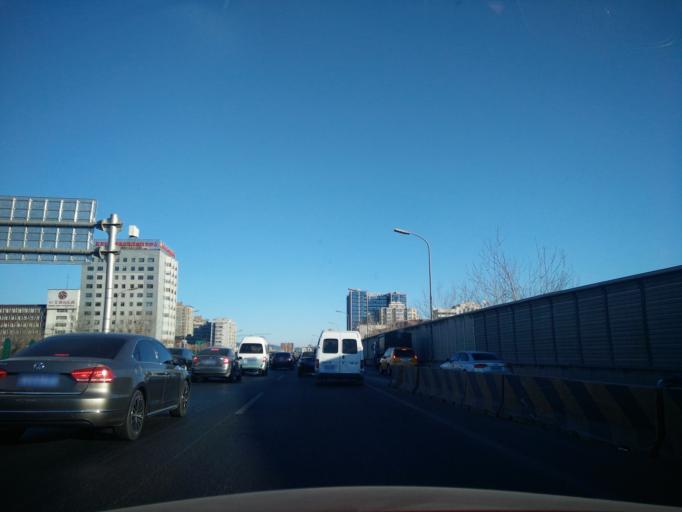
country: CN
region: Beijing
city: Lugu
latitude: 39.8961
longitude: 116.2051
